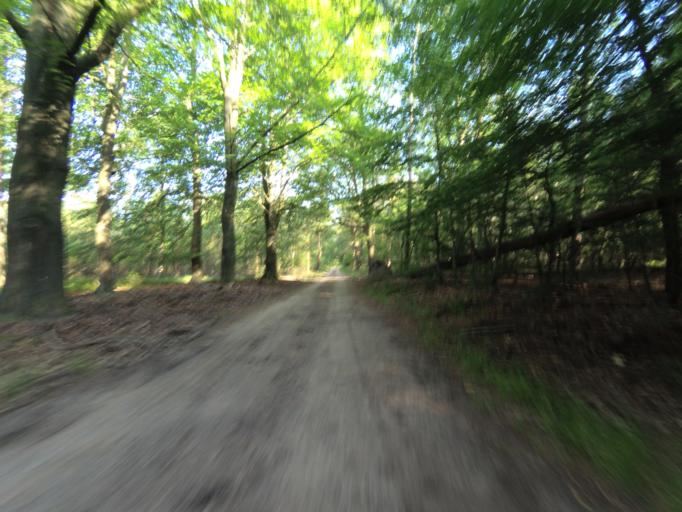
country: NL
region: Gelderland
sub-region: Gemeente Apeldoorn
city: Beekbergen
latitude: 52.1669
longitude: 5.8715
